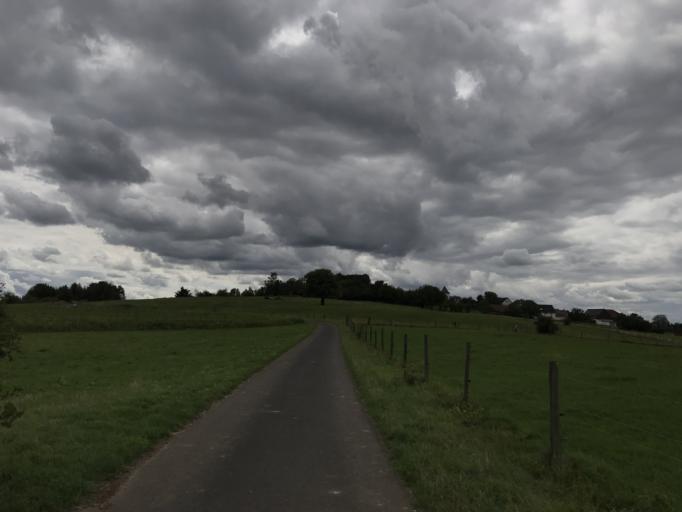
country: DE
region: Hesse
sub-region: Regierungsbezirk Giessen
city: Grunberg
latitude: 50.6216
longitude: 8.9714
